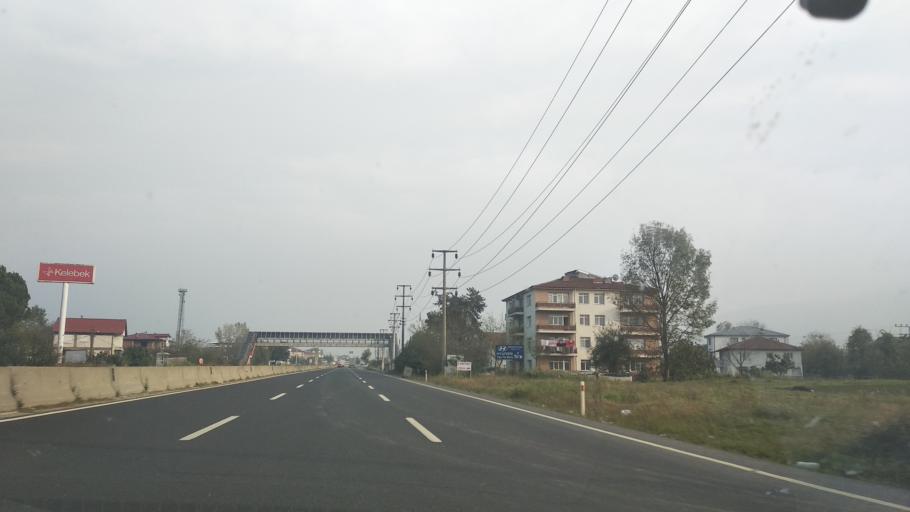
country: TR
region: Duzce
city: Duzce
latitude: 40.8065
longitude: 31.2310
